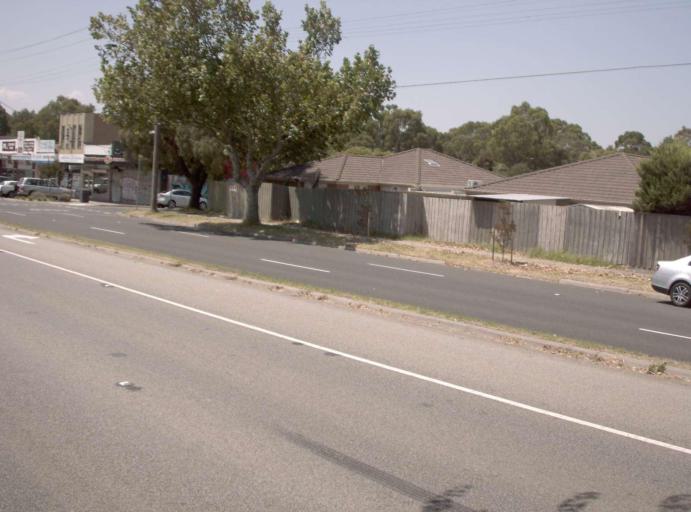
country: AU
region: Victoria
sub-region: Greater Dandenong
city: Springvale
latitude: -37.9433
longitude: 145.1538
